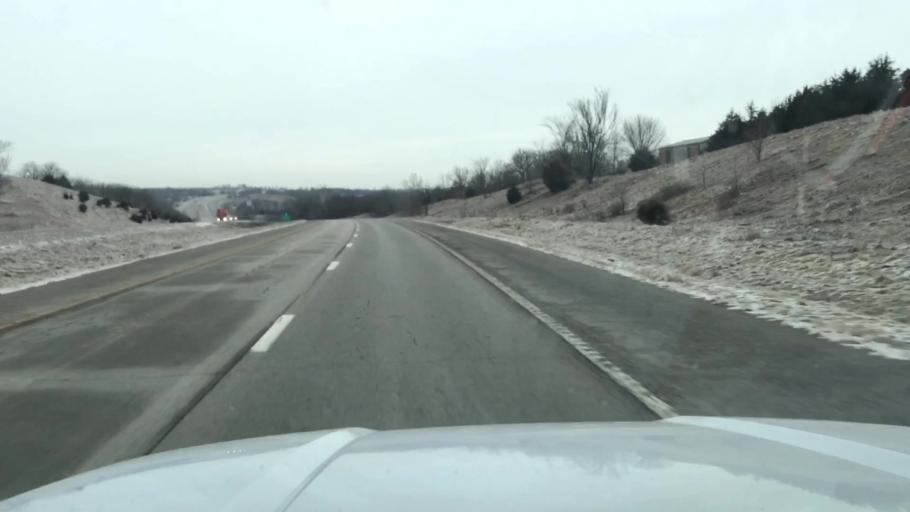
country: US
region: Missouri
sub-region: Andrew County
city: Savannah
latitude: 39.8999
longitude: -94.8570
